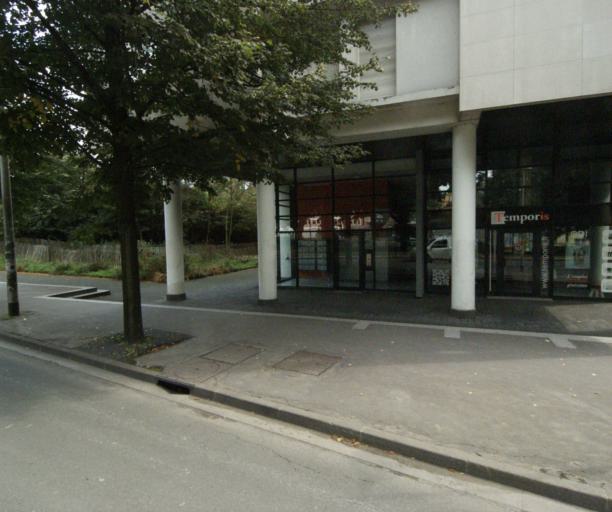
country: FR
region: Nord-Pas-de-Calais
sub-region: Departement du Nord
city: La Madeleine
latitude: 50.6416
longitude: 3.0712
